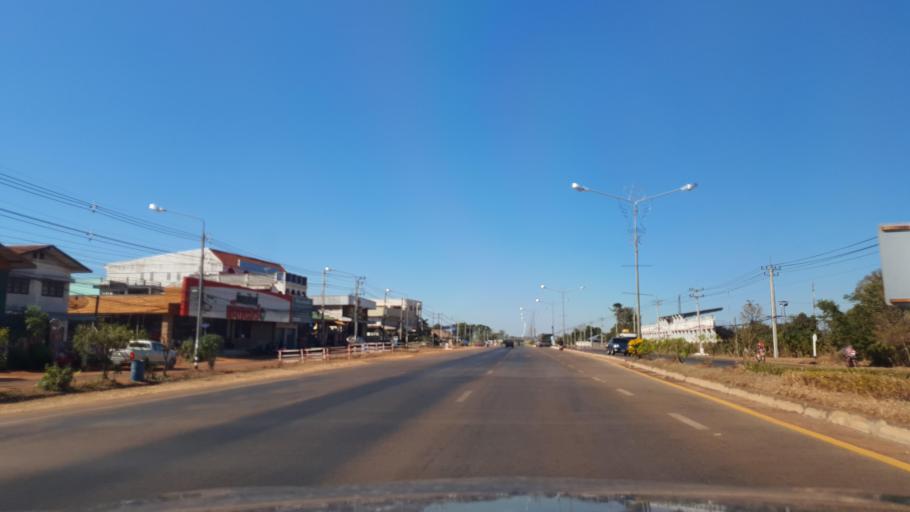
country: TH
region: Sakon Nakhon
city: Sakon Nakhon
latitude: 17.2562
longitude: 104.1819
